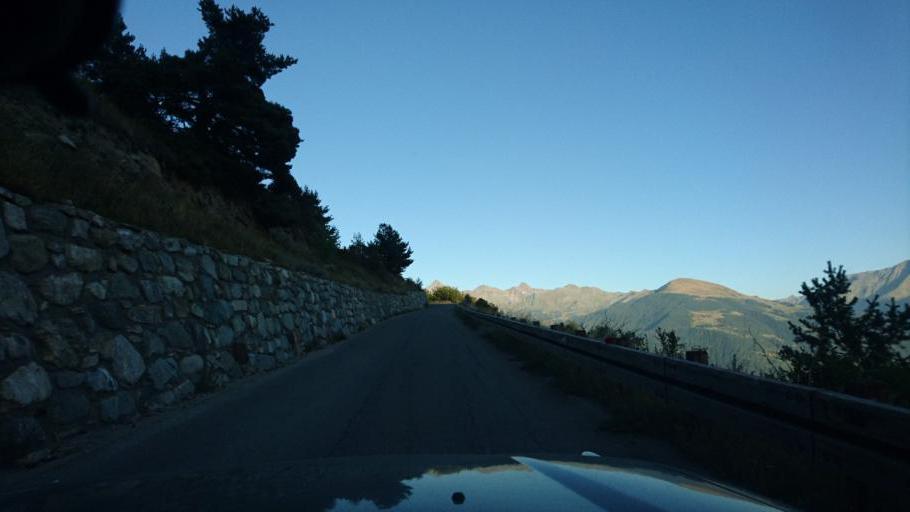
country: IT
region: Aosta Valley
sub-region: Valle d'Aosta
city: Saint-Nicolas
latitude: 45.7282
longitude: 7.1849
